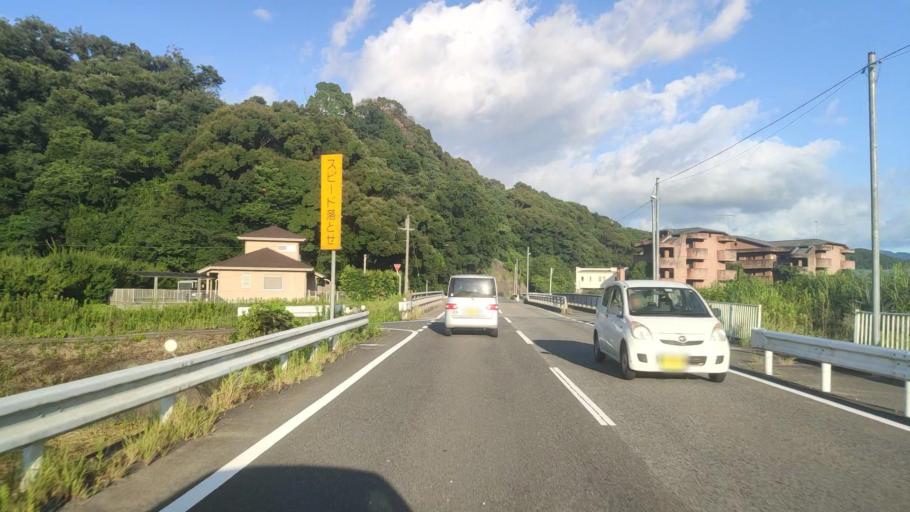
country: JP
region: Wakayama
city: Tanabe
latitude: 33.7262
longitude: 135.4427
